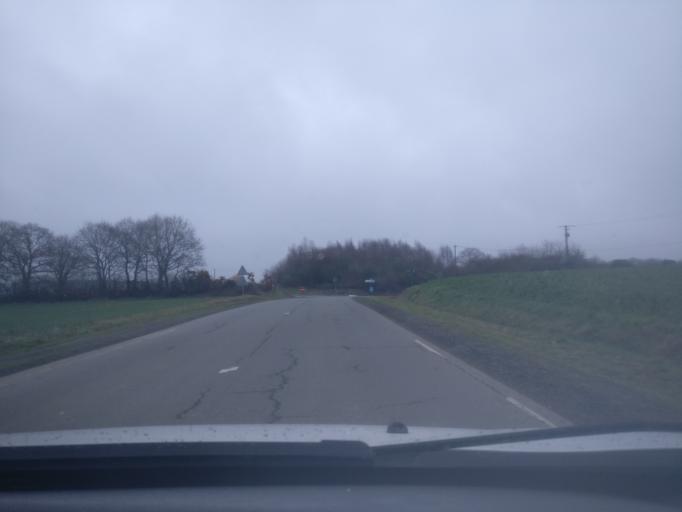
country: FR
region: Brittany
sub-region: Departement d'Ille-et-Vilaine
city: Chasne-sur-Illet
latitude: 48.2900
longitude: -1.5830
